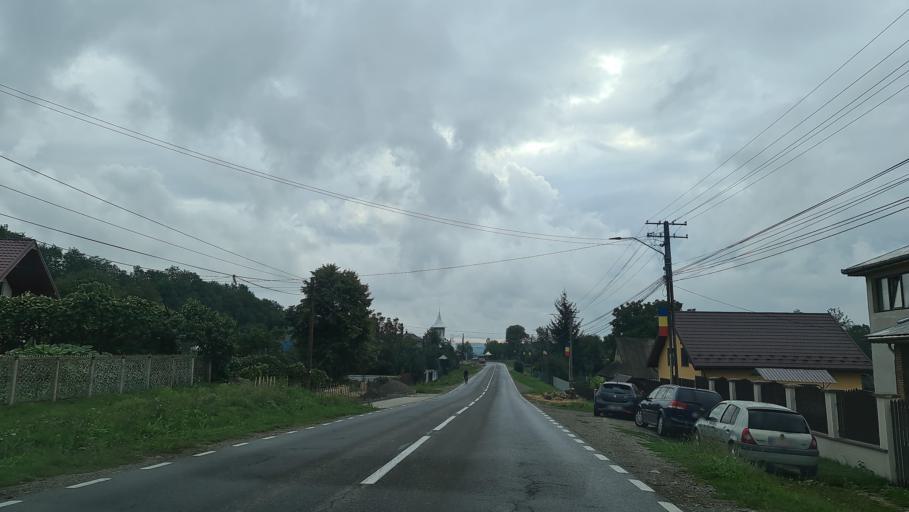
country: RO
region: Neamt
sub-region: Comuna Borlesti
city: Ruseni
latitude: 46.7942
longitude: 26.5339
